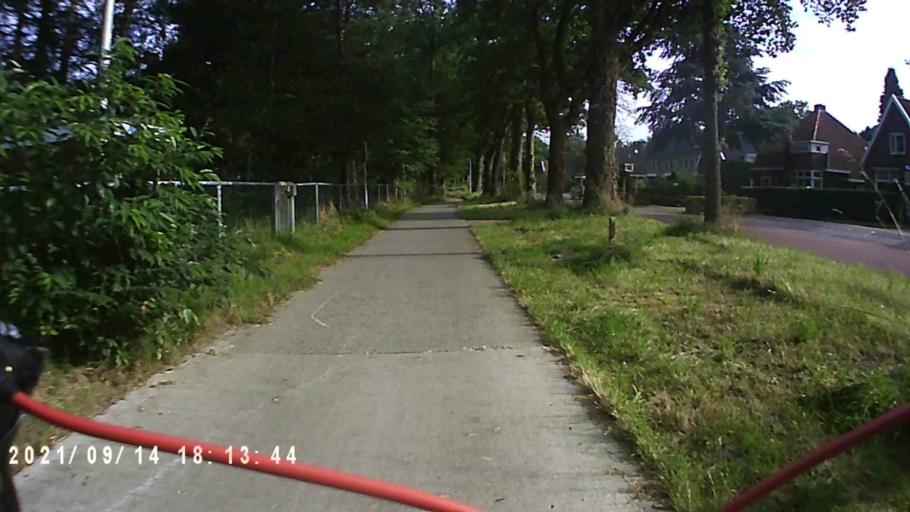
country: NL
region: Drenthe
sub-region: Gemeente Tynaarlo
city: Zuidlaren
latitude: 53.0879
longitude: 6.6667
